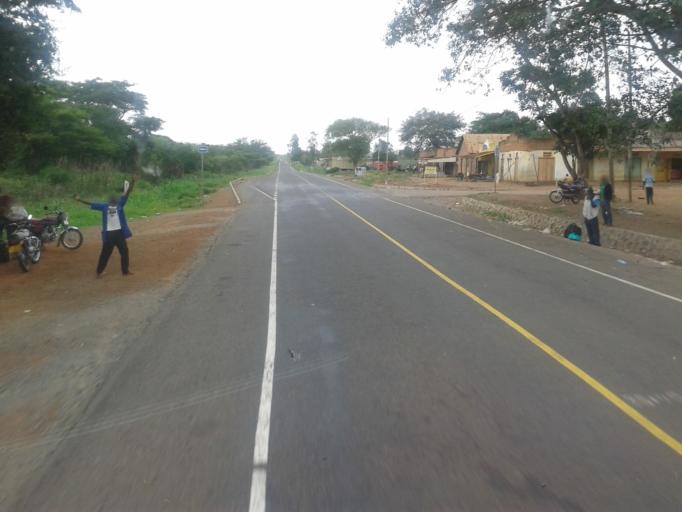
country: UG
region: Northern Region
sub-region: Oyam District
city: Oyam
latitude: 2.1647
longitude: 32.2196
